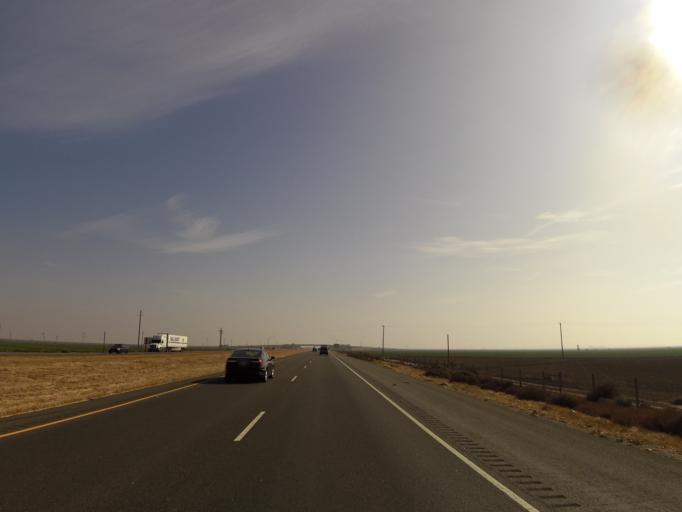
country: US
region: California
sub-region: Kern County
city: Greenfield
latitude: 35.1674
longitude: -119.1175
